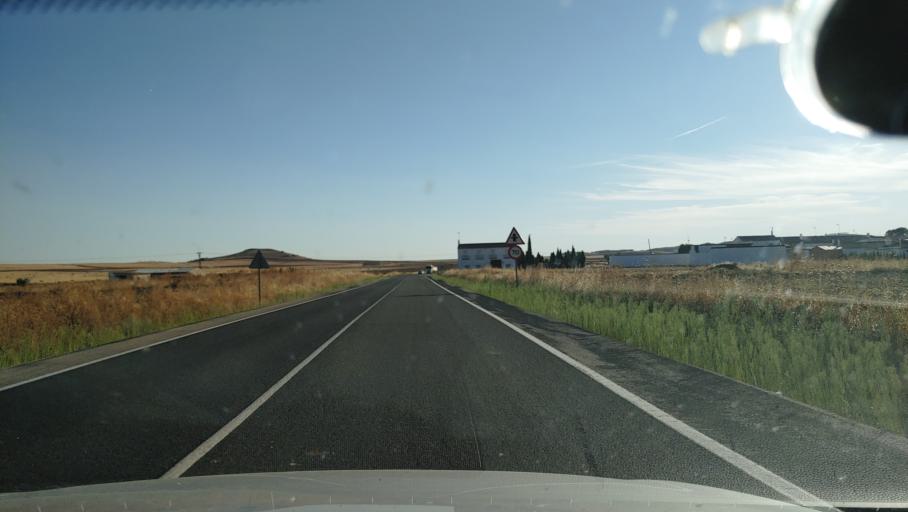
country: ES
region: Castille-La Mancha
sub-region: Provincia de Ciudad Real
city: Fuenllana
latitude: 38.7553
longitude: -2.9532
